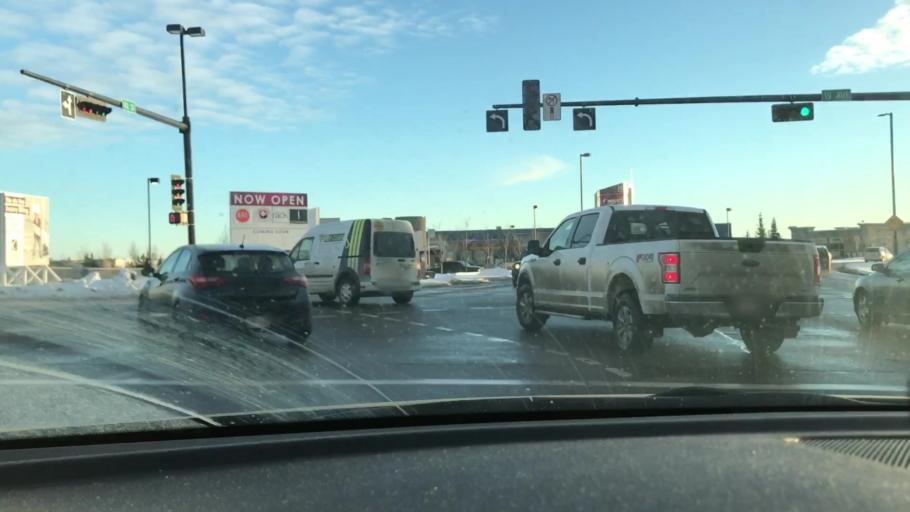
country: CA
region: Alberta
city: Edmonton
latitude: 53.4468
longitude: -113.4905
